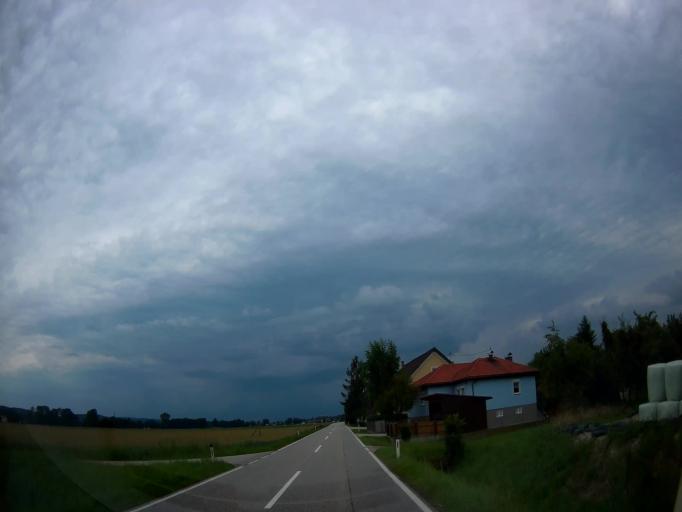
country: AT
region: Upper Austria
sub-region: Politischer Bezirk Braunau am Inn
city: Braunau am Inn
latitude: 48.1772
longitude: 13.1280
